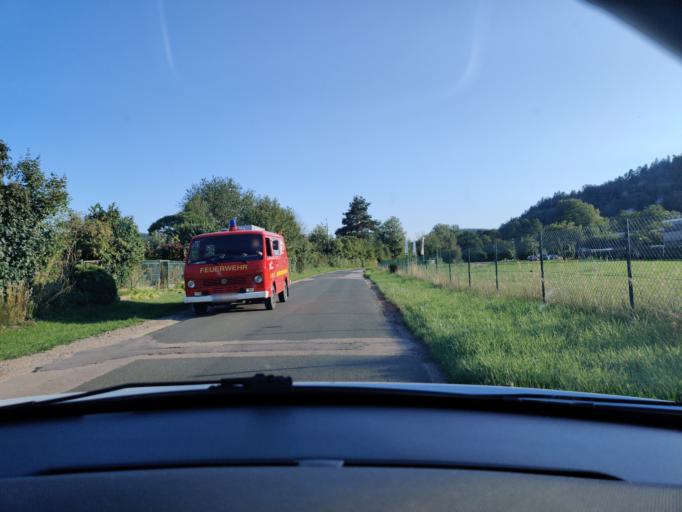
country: DE
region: Bavaria
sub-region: Upper Palatinate
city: Nabburg
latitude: 49.4449
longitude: 12.1773
